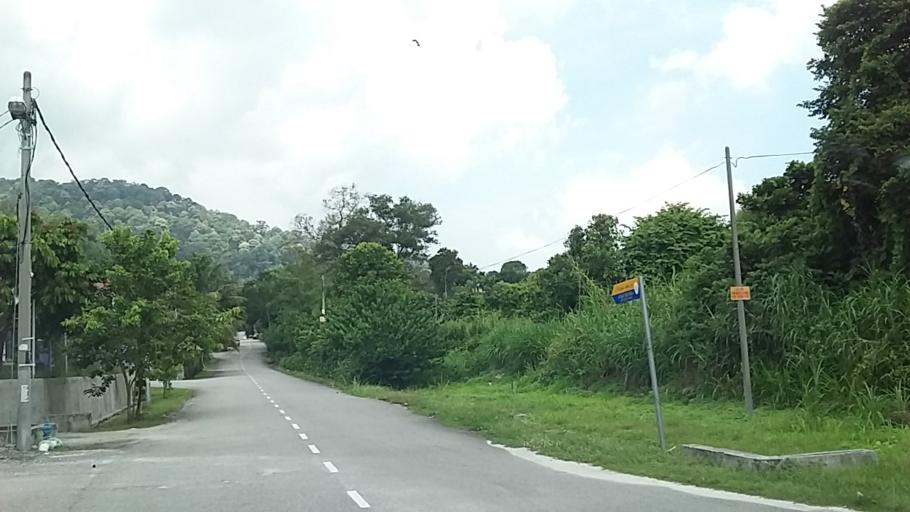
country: MY
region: Johor
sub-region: Daerah Batu Pahat
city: Batu Pahat
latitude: 1.8374
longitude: 102.9462
